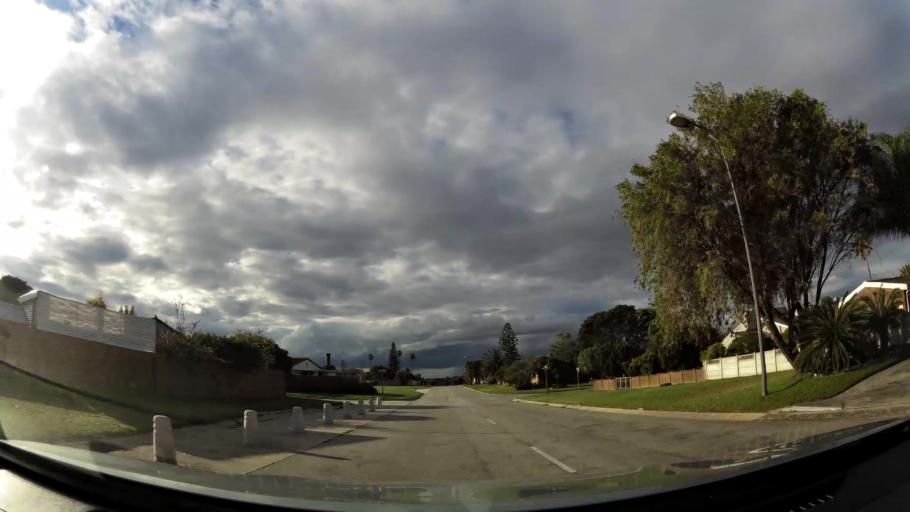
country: ZA
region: Eastern Cape
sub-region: Nelson Mandela Bay Metropolitan Municipality
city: Port Elizabeth
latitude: -33.9574
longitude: 25.4799
